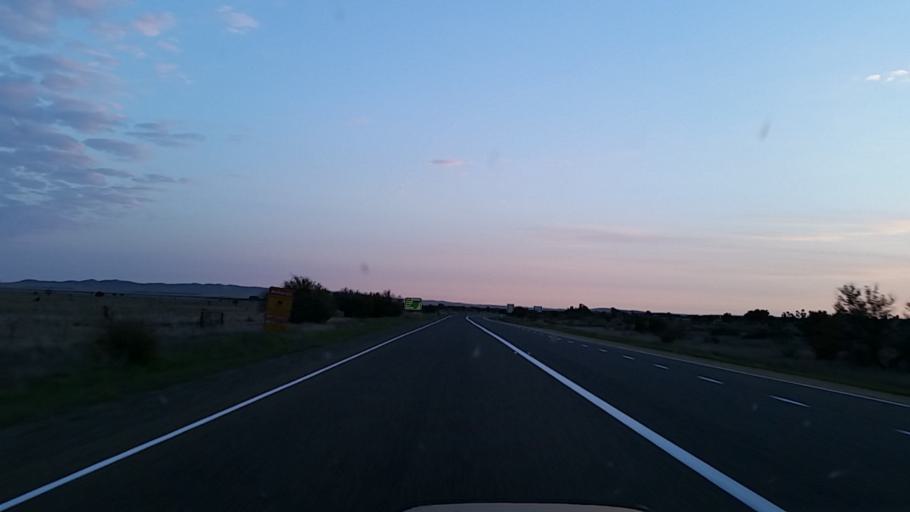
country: AU
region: South Australia
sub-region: Peterborough
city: Peterborough
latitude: -33.1355
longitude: 138.9342
